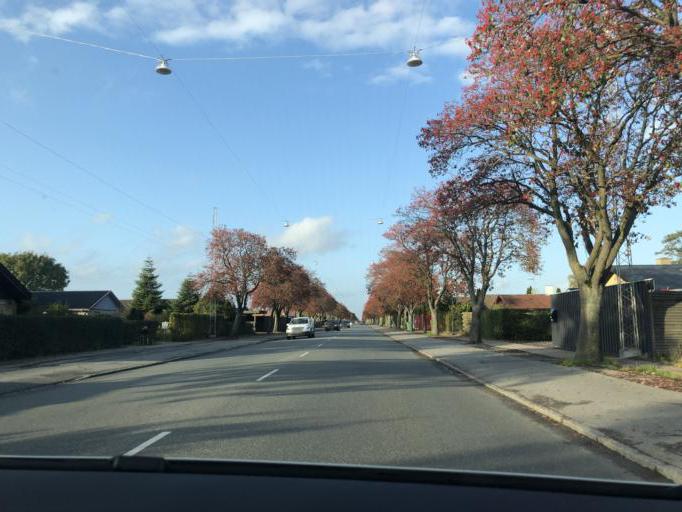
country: DK
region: Capital Region
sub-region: Tarnby Kommune
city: Tarnby
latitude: 55.6002
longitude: 12.5828
